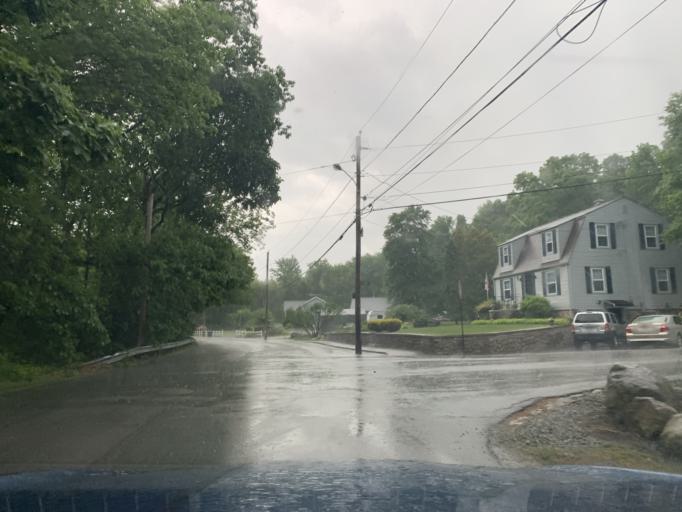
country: US
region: Rhode Island
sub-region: Kent County
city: West Warwick
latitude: 41.7309
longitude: -71.5509
